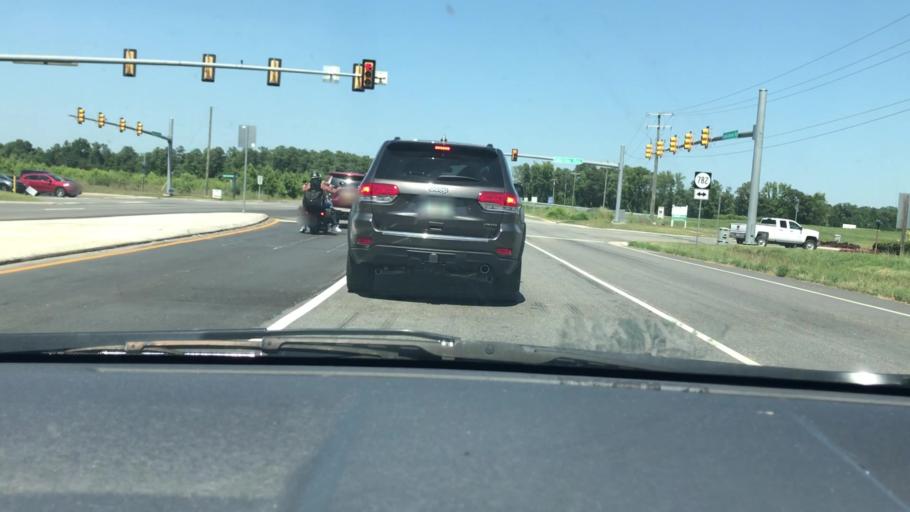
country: US
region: Virginia
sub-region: Hanover County
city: Ashland
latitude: 37.7189
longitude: -77.4537
